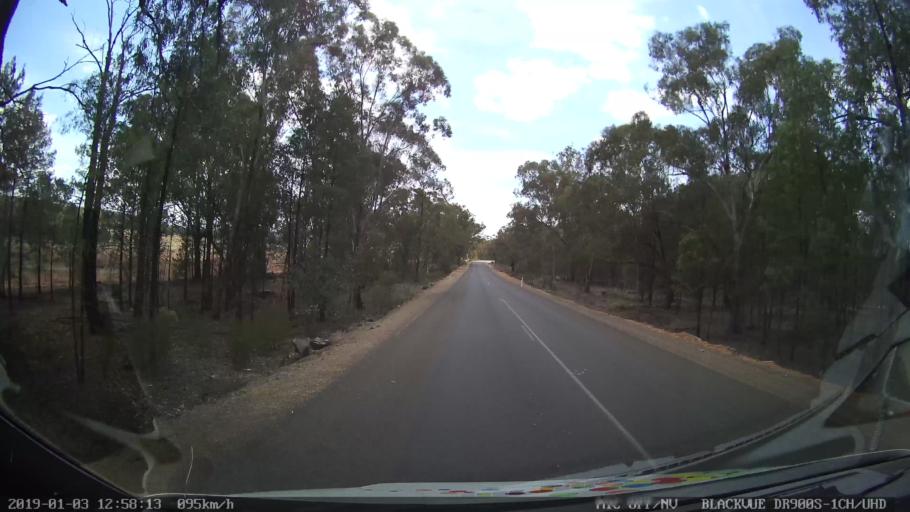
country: AU
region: New South Wales
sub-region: Cabonne
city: Canowindra
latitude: -33.6439
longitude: 148.3723
